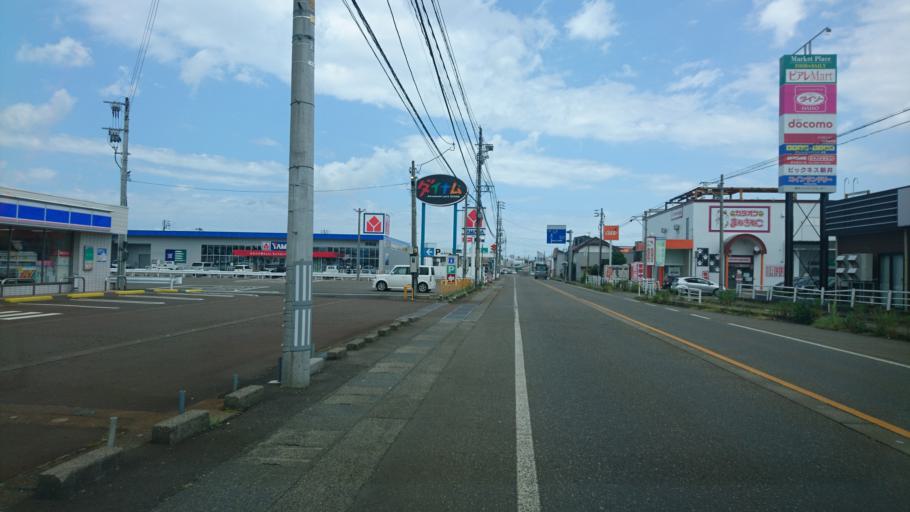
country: JP
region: Niigata
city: Arai
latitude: 37.0541
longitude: 138.2605
